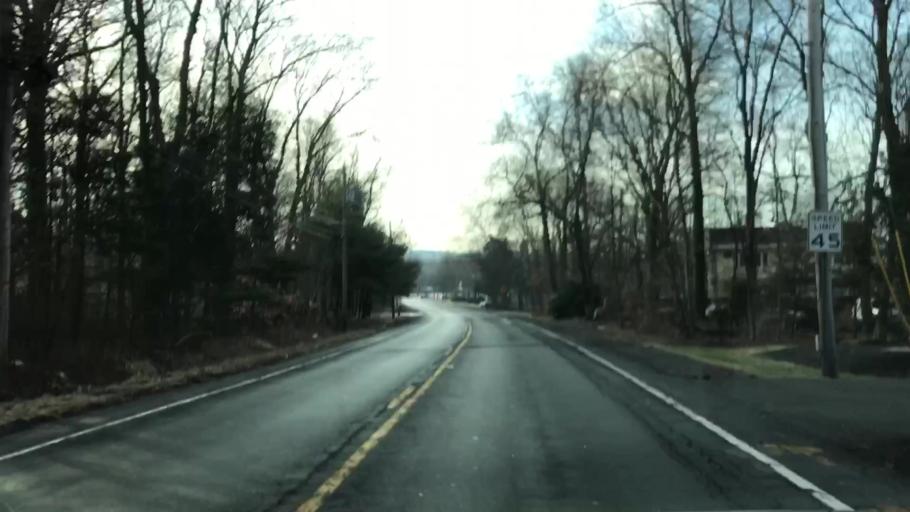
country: US
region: New York
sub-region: Rockland County
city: Congers
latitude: 41.1505
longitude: -73.9350
